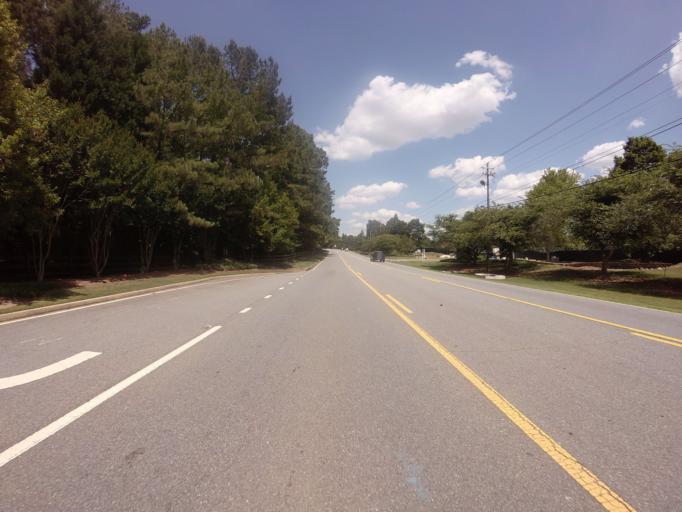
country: US
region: Georgia
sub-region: Fulton County
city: Johns Creek
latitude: 34.0082
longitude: -84.2127
